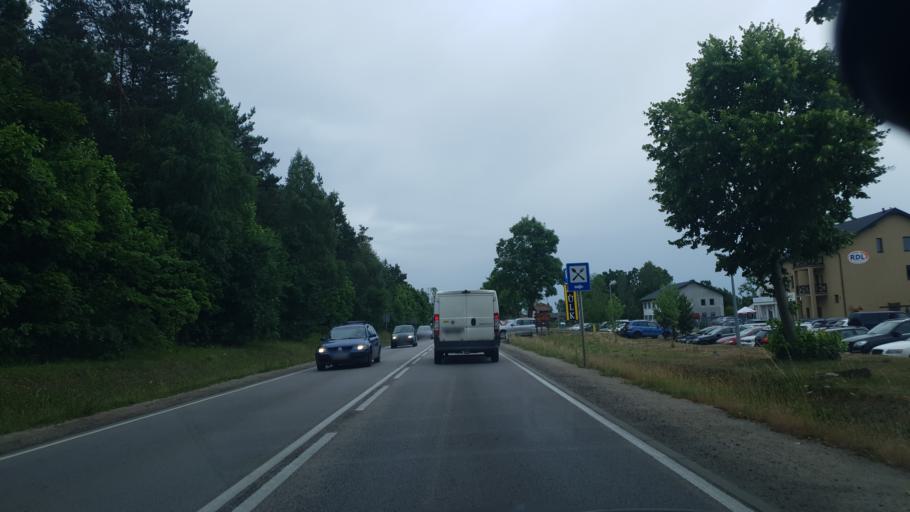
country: PL
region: Pomeranian Voivodeship
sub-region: Powiat kartuski
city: Banino
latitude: 54.4000
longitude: 18.3590
